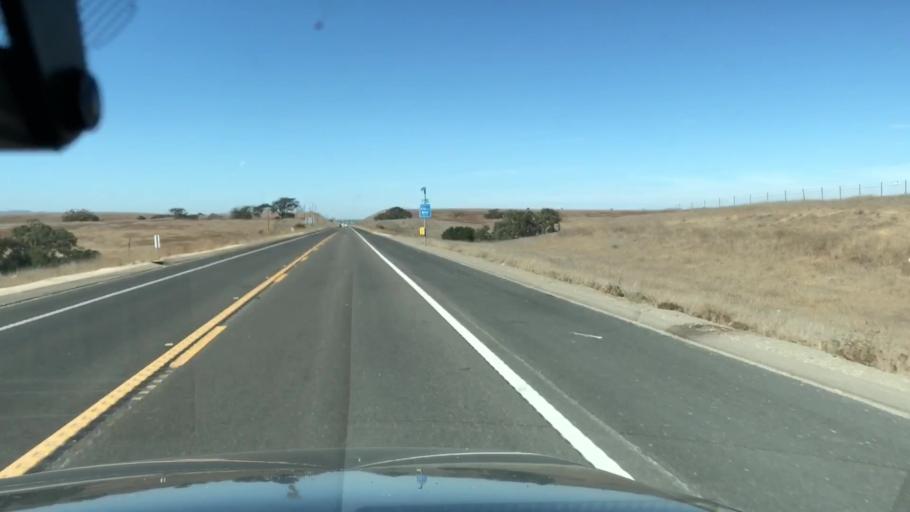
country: US
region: California
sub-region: Santa Barbara County
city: Santa Ynez
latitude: 34.6005
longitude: -120.0442
